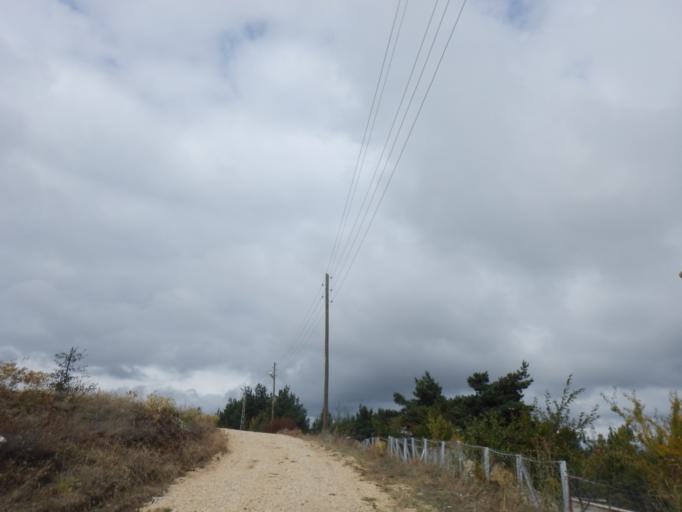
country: TR
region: Ordu
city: Mesudiye
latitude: 40.4308
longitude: 37.7798
